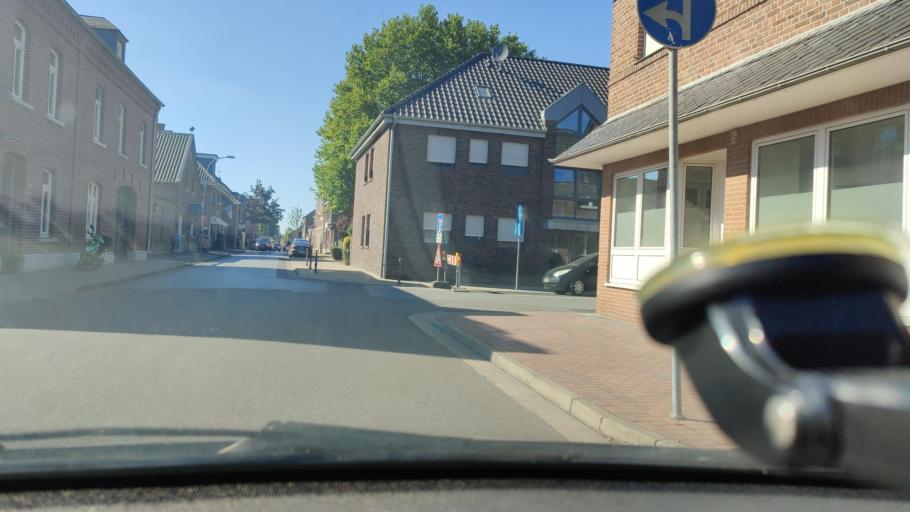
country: DE
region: North Rhine-Westphalia
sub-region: Regierungsbezirk Dusseldorf
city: Wachtendonk
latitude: 51.4565
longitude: 6.3711
